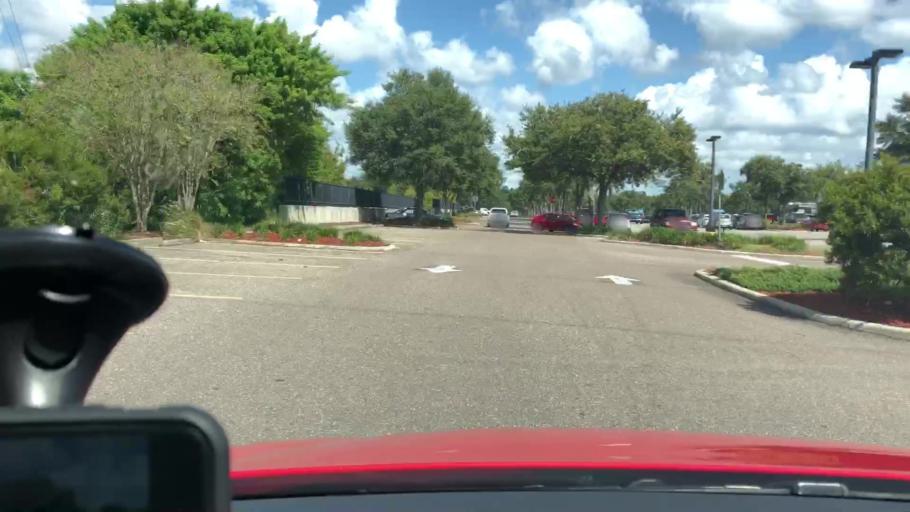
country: US
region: Florida
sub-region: Volusia County
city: Deltona
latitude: 28.9123
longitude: -81.2807
